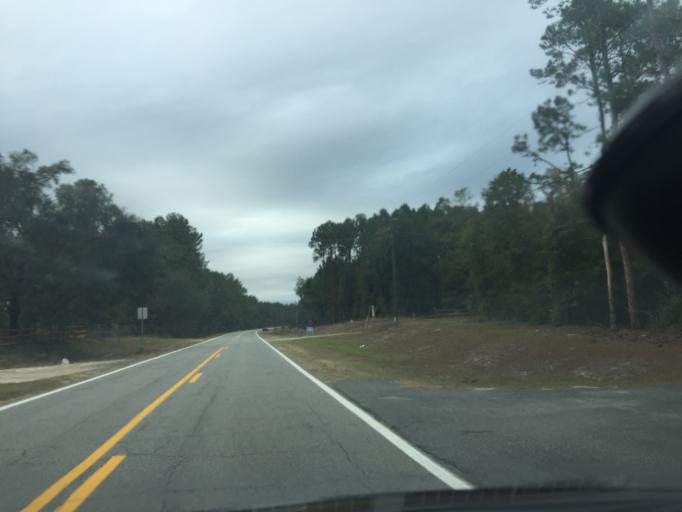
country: US
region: Georgia
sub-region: Chatham County
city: Bloomingdale
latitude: 32.0962
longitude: -81.3785
